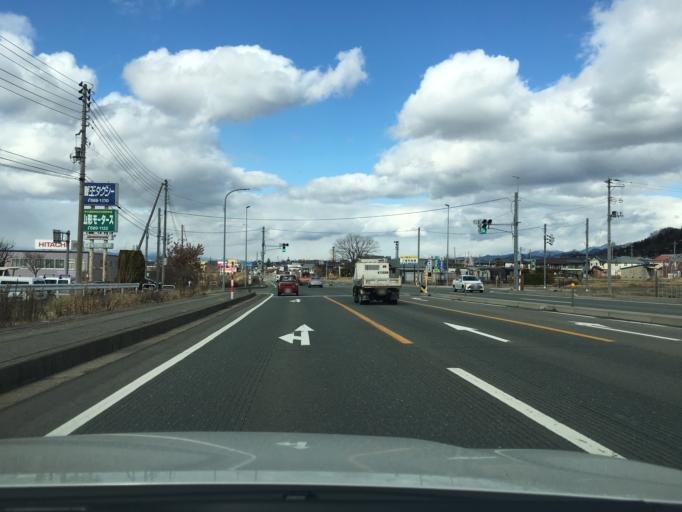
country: JP
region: Yamagata
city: Kaminoyama
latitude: 38.1979
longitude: 140.3144
